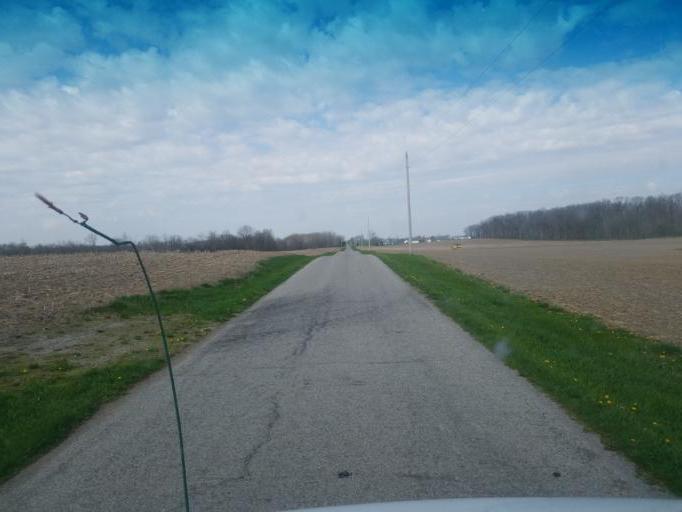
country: US
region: Ohio
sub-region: Logan County
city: Northwood
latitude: 40.4923
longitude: -83.7202
